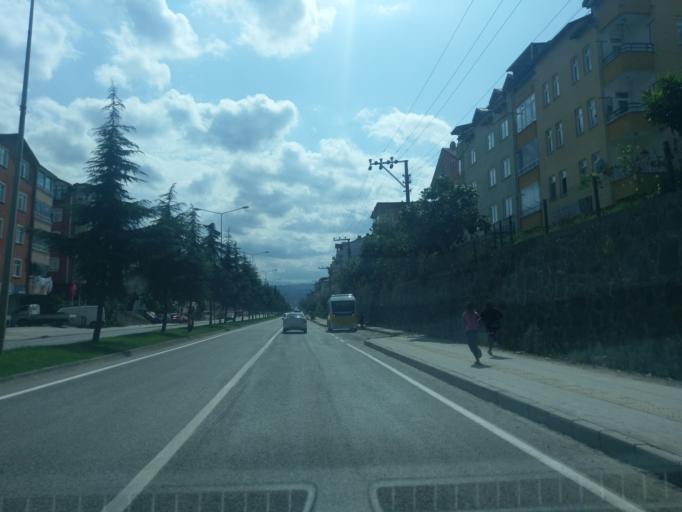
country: TR
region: Ordu
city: Ordu
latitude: 40.9633
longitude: 37.8993
